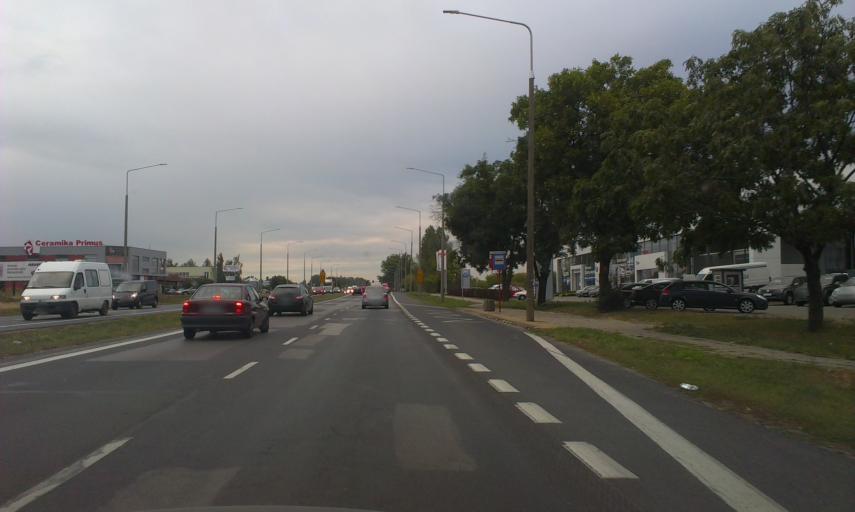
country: PL
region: Masovian Voivodeship
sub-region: Radom
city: Radom
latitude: 51.4485
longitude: 21.1437
